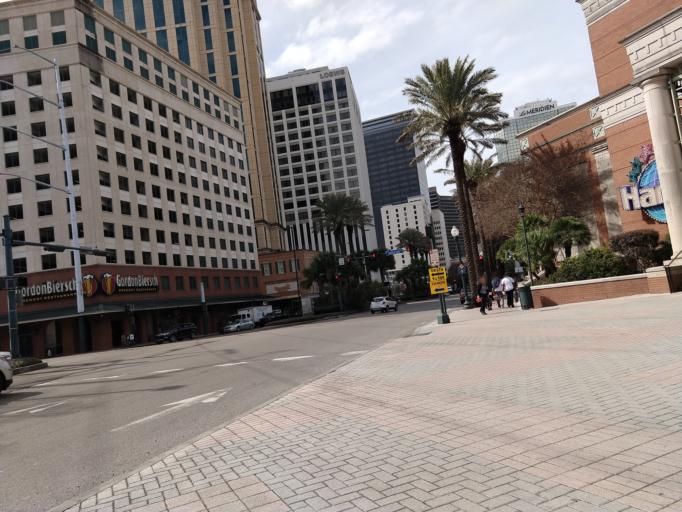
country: US
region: Louisiana
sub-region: Orleans Parish
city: New Orleans
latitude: 29.9484
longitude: -90.0644
